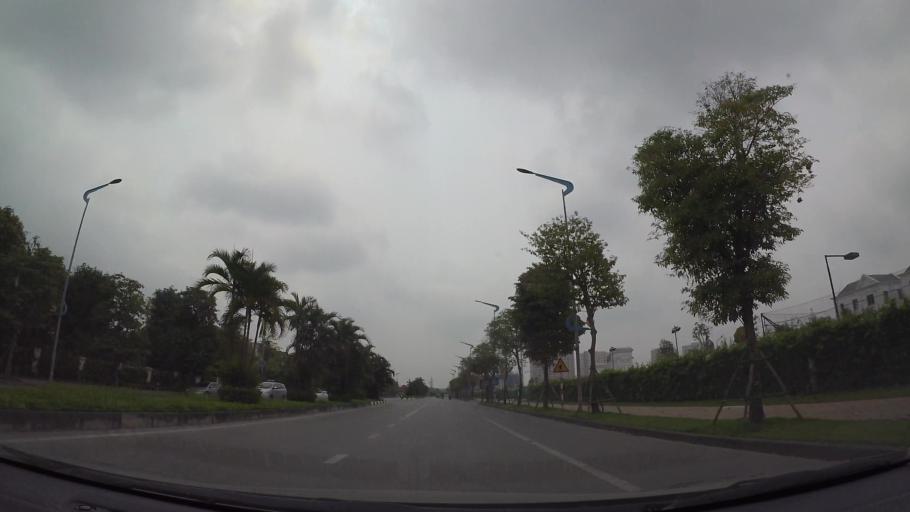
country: VN
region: Ha Noi
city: Trau Quy
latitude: 21.0447
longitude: 105.9113
